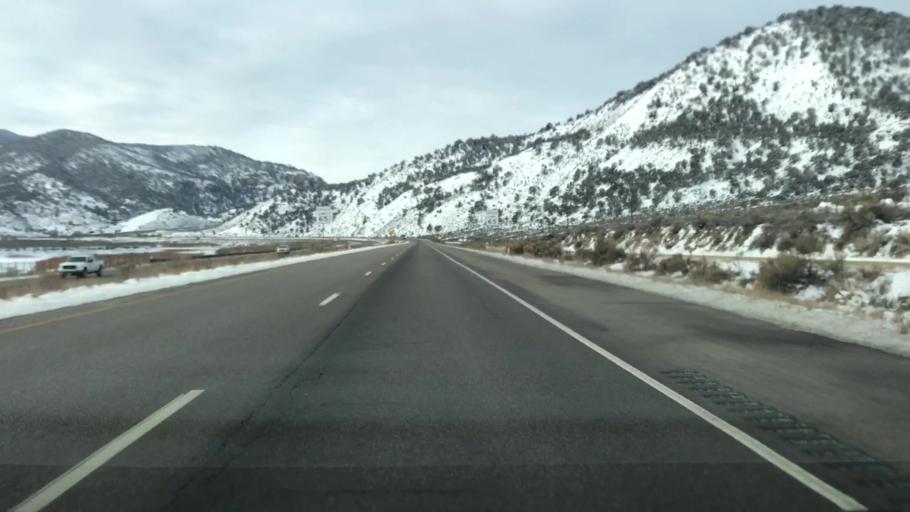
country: US
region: Colorado
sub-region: Eagle County
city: Gypsum
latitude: 39.6369
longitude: -107.0950
